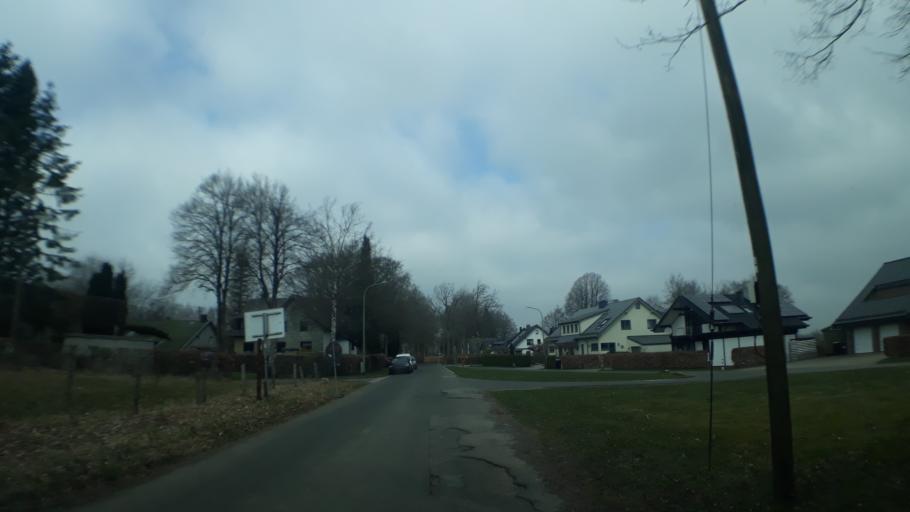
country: DE
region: North Rhine-Westphalia
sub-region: Regierungsbezirk Koln
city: Monschau
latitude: 50.5072
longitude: 6.2321
